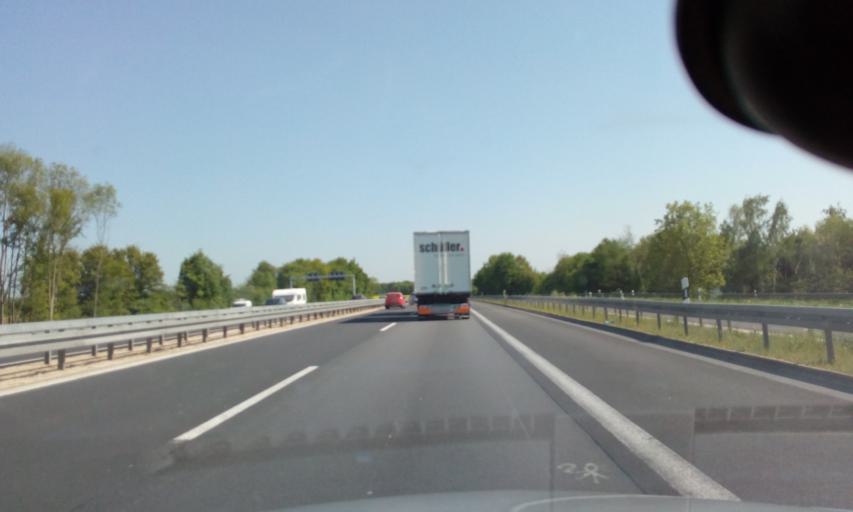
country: DE
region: North Rhine-Westphalia
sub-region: Regierungsbezirk Koln
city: Kerpen
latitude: 50.8581
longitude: 6.7188
